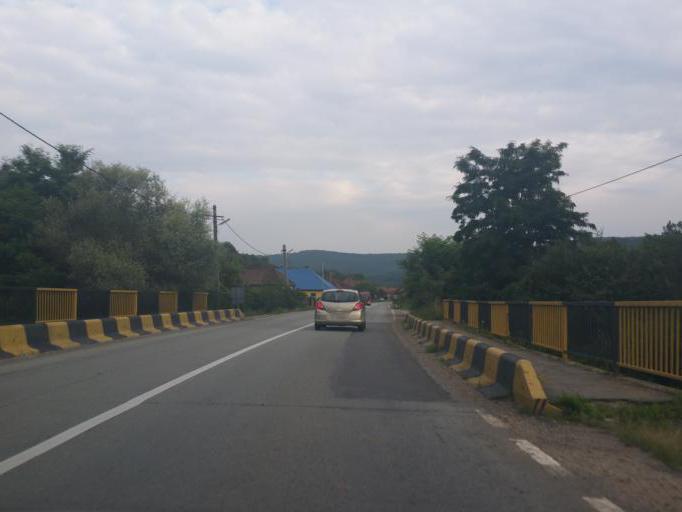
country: RO
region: Salaj
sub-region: Comuna Zimbor
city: Zimbor
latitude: 46.9897
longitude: 23.2516
